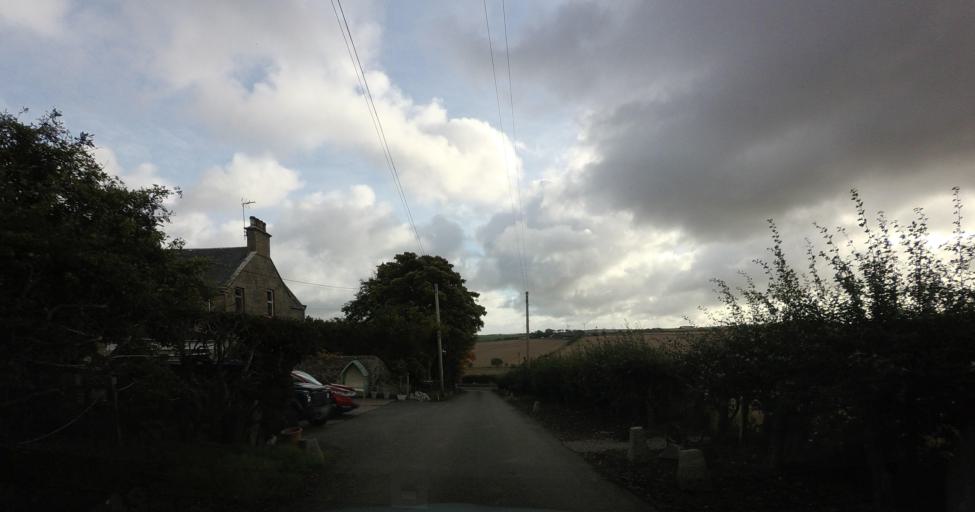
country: GB
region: Scotland
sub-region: Aberdeenshire
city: Whitehills
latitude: 57.6551
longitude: -2.6141
